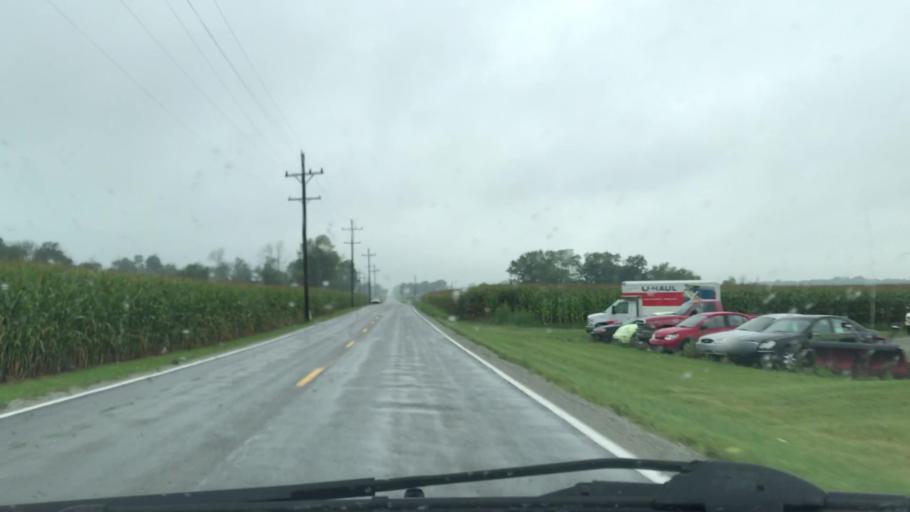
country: US
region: Indiana
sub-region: Hamilton County
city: Sheridan
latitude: 40.1297
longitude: -86.2388
